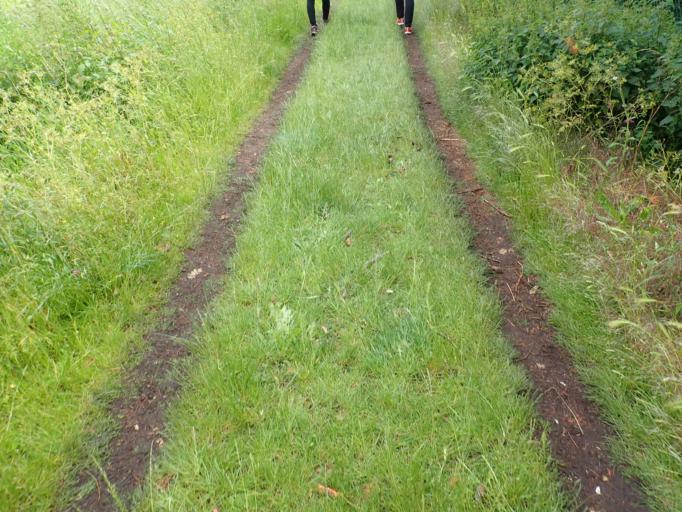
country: BE
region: Flanders
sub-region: Provincie Antwerpen
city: Heist-op-den-Berg
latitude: 51.1005
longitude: 4.7362
